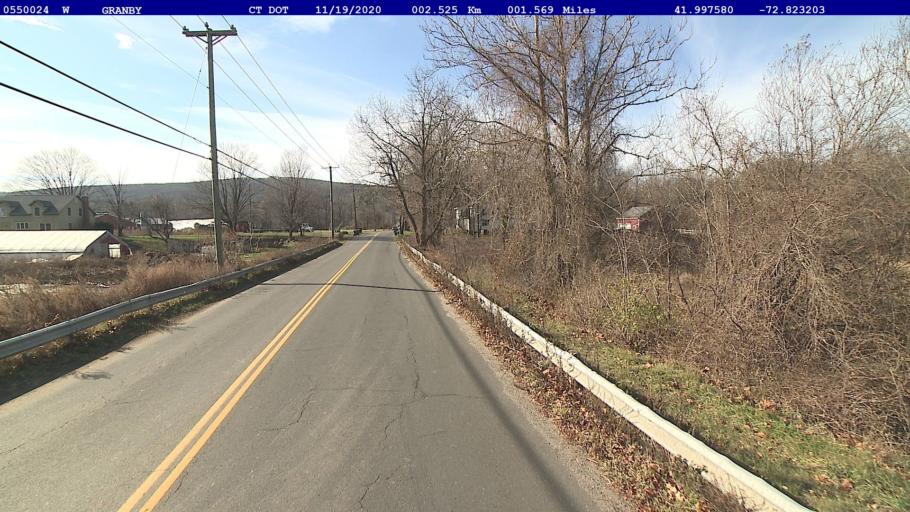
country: US
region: Connecticut
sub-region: Hartford County
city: North Granby
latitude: 41.9976
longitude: -72.8232
